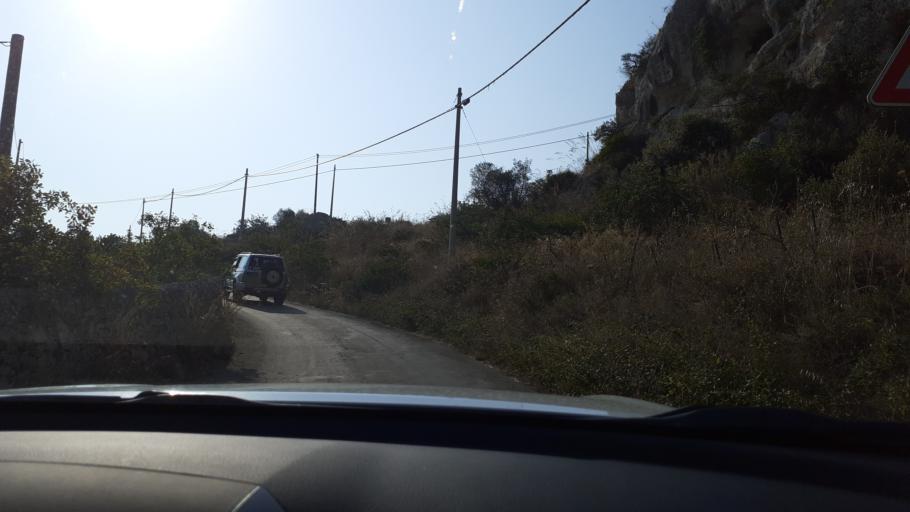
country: IT
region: Sicily
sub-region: Provincia di Siracusa
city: Cassibile
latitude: 36.9782
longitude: 15.1594
